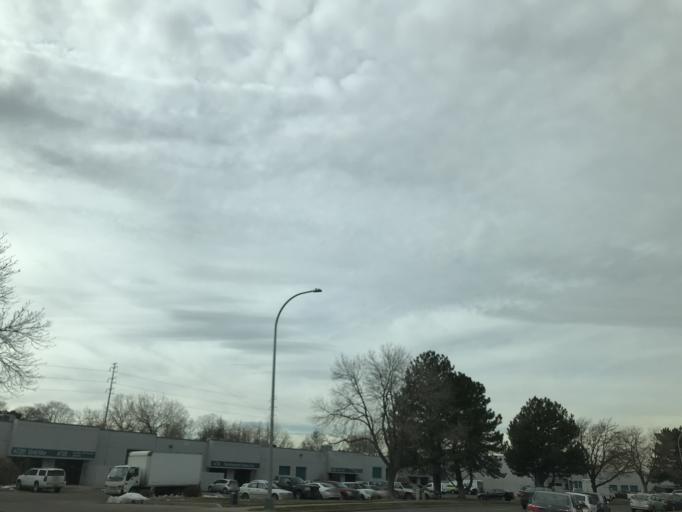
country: US
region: Colorado
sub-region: Adams County
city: Commerce City
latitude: 39.7824
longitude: -104.9100
